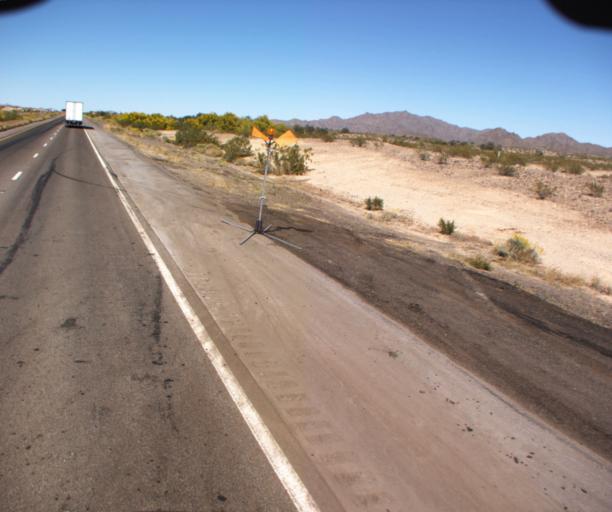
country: US
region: Arizona
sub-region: Maricopa County
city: Gila Bend
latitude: 33.0815
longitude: -112.6471
